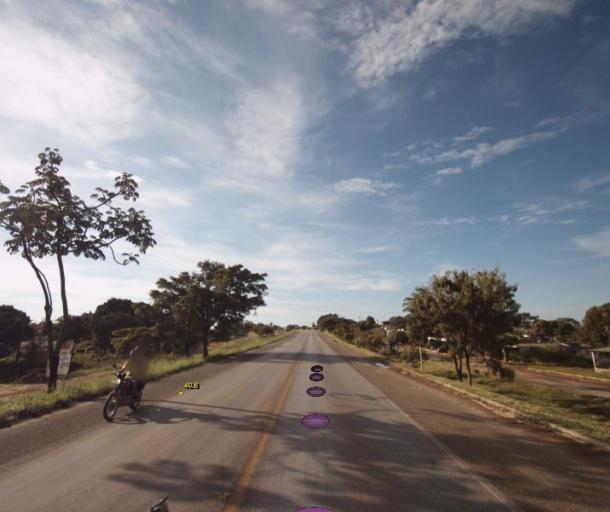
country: BR
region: Goias
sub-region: Pirenopolis
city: Pirenopolis
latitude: -15.7763
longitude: -48.5394
